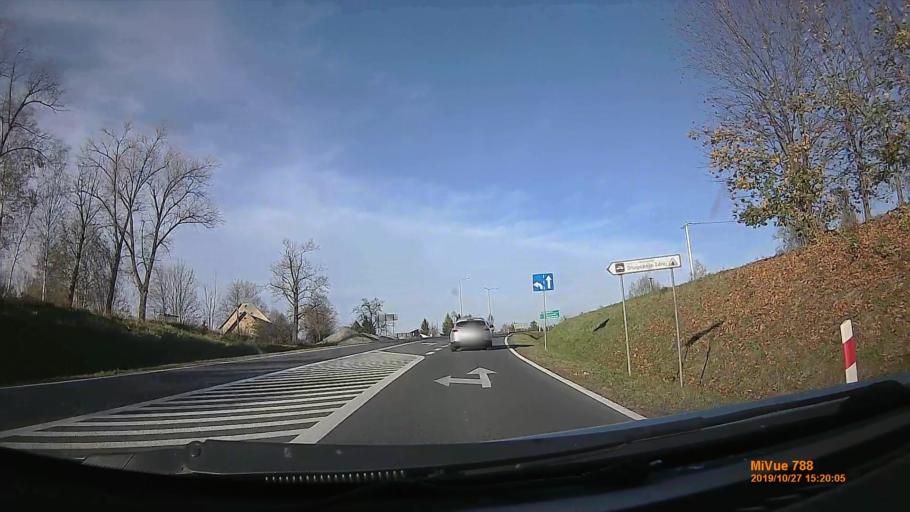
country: PL
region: Lower Silesian Voivodeship
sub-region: Powiat klodzki
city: Bystrzyca Klodzka
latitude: 50.2789
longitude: 16.6487
